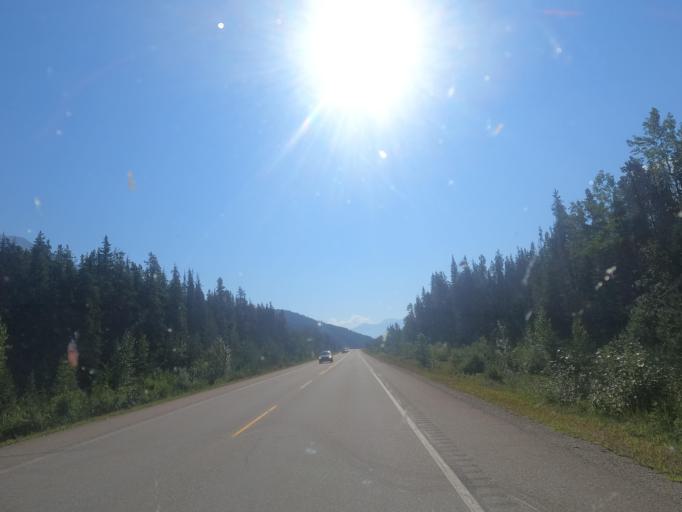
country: CA
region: Alberta
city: Jasper Park Lodge
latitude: 52.9218
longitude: -118.8075
